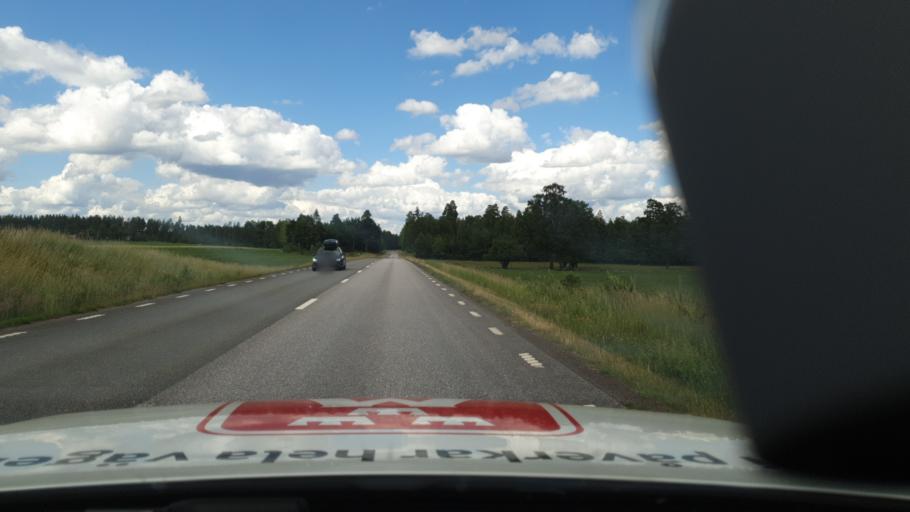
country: SE
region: Vaestra Goetaland
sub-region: Karlsborgs Kommun
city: Molltorp
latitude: 58.4567
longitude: 14.4038
